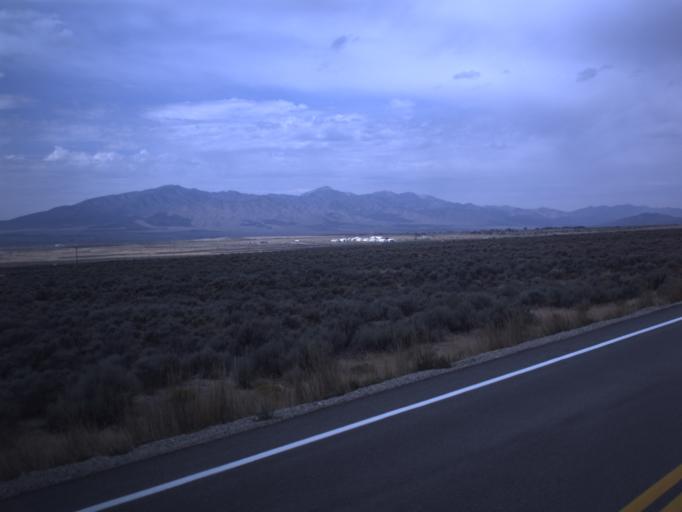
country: US
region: Utah
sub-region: Tooele County
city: Tooele
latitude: 40.2985
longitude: -112.2754
